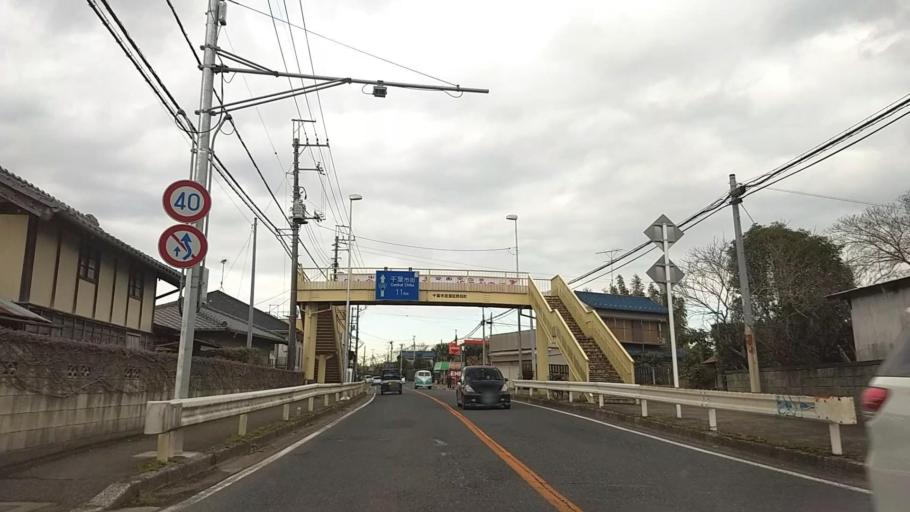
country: JP
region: Chiba
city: Yotsukaido
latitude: 35.5822
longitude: 140.2319
